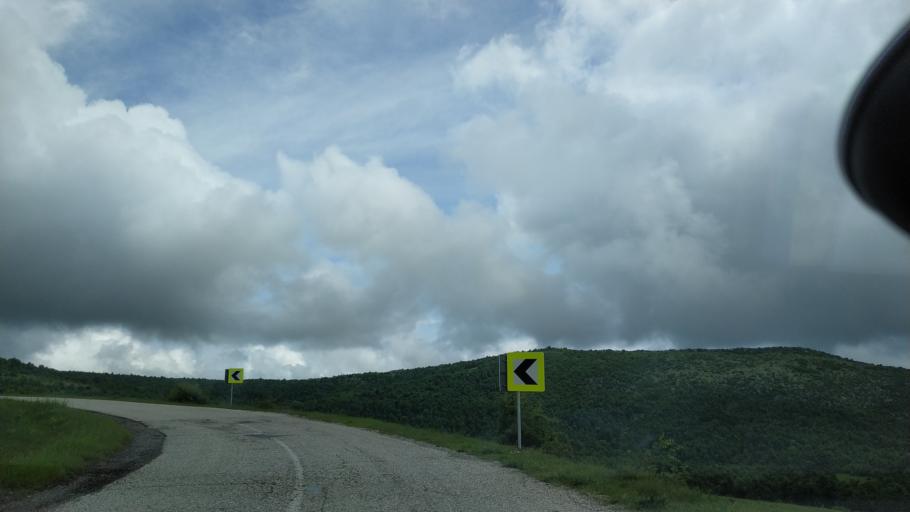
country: RS
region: Central Serbia
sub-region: Zajecarski Okrug
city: Soko Banja
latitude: 43.7089
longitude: 21.9405
